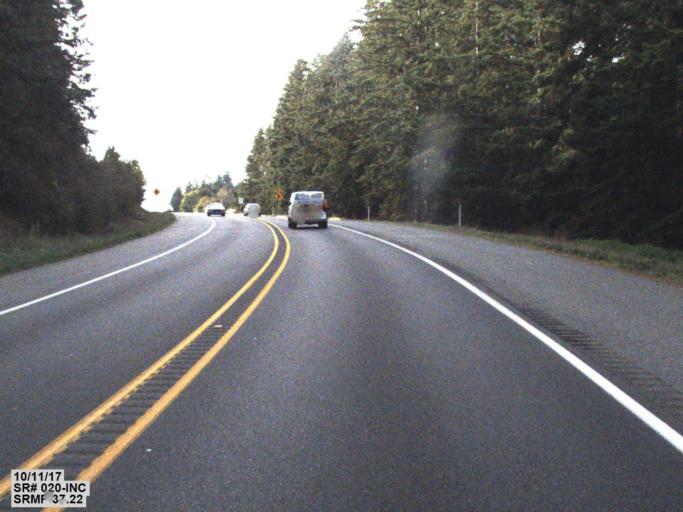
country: US
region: Washington
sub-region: Island County
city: Ault Field
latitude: 48.3580
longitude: -122.6170
